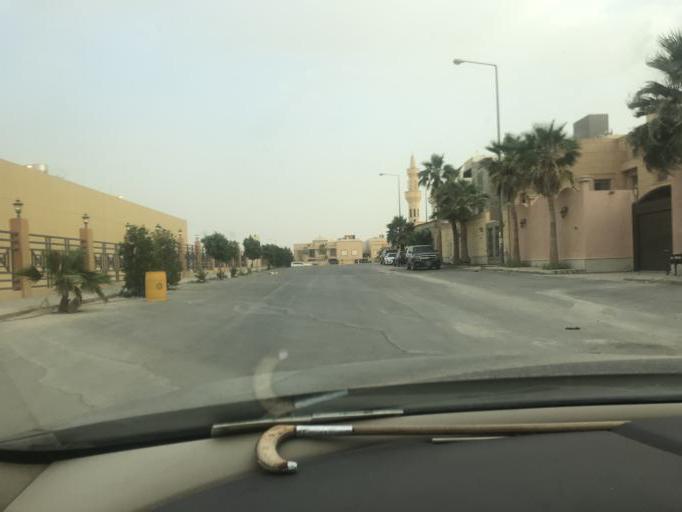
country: SA
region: Ar Riyad
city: Riyadh
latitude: 24.8080
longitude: 46.6683
